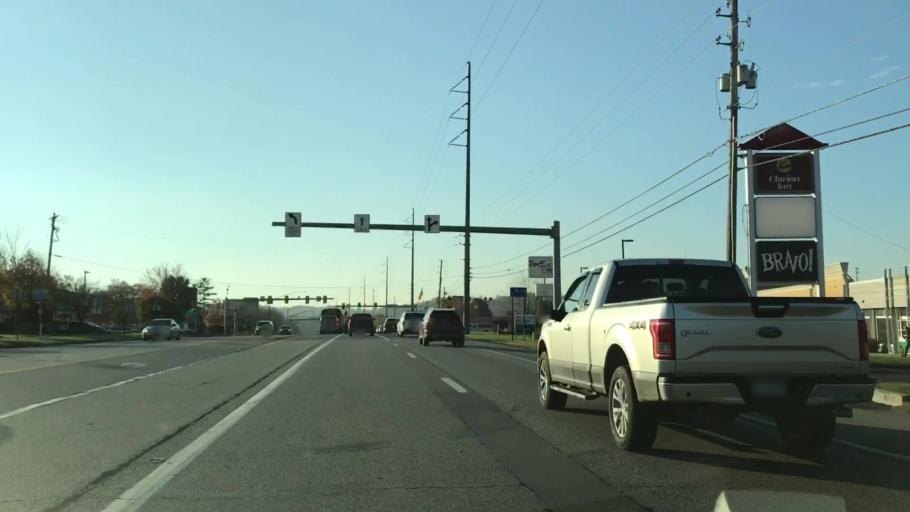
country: US
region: Pennsylvania
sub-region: Butler County
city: Cranberry Township
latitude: 40.6749
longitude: -80.0989
